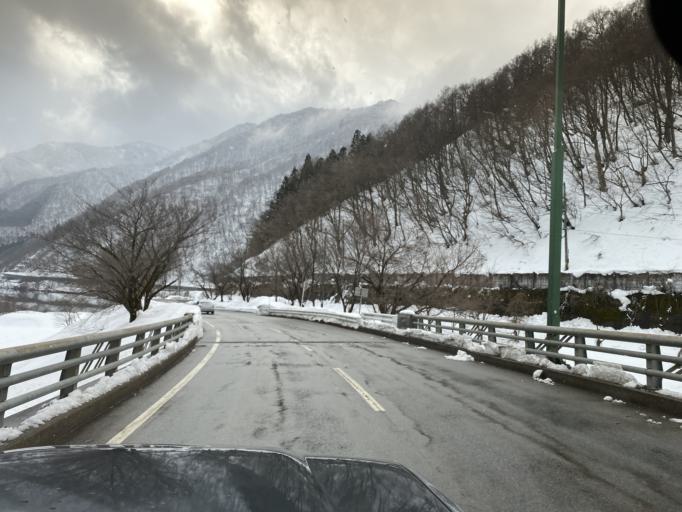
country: JP
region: Toyama
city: Fukumitsu
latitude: 36.2300
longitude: 136.8792
